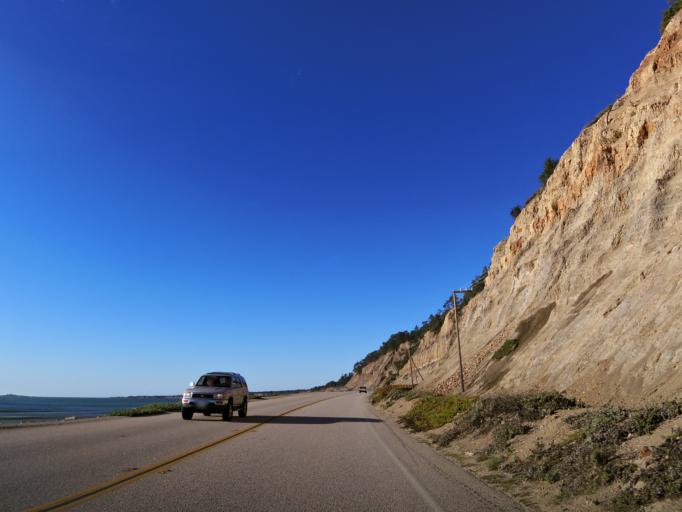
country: US
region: California
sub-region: Santa Cruz County
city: Bonny Doon
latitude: 37.0986
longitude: -122.2821
